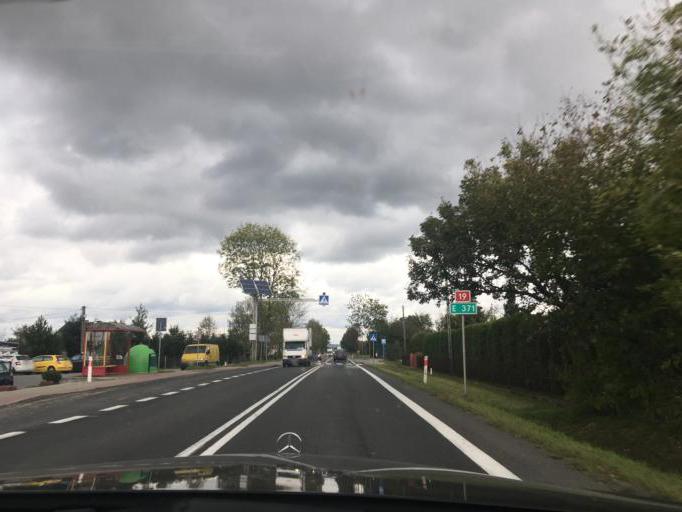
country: PL
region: Subcarpathian Voivodeship
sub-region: Powiat krosnienski
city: Miejsce Piastowe
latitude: 49.6468
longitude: 21.8116
